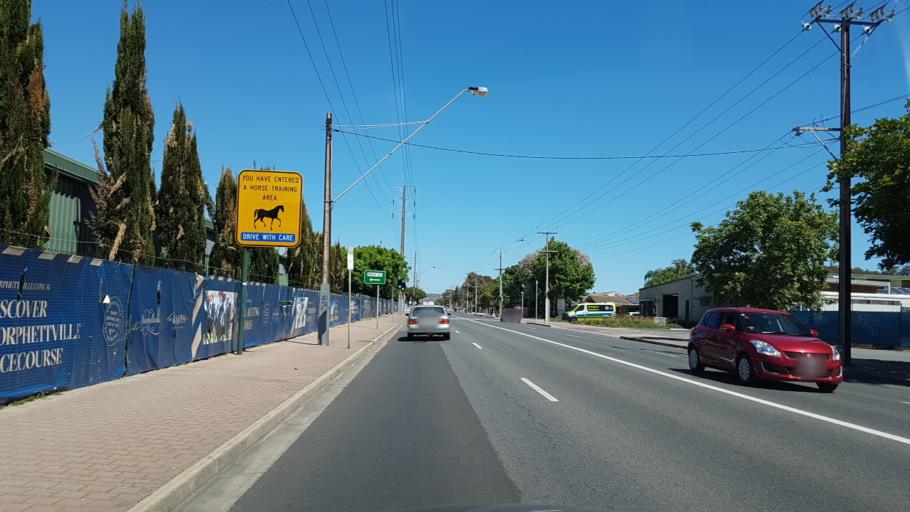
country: AU
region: South Australia
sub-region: Marion
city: Plympton Park
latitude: -34.9798
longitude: 138.5381
